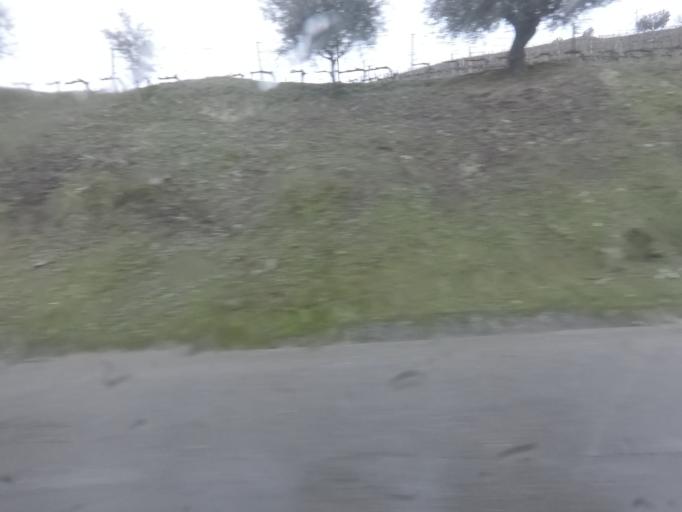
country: PT
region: Vila Real
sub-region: Peso da Regua
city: Peso da Regua
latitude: 41.1712
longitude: -7.7656
